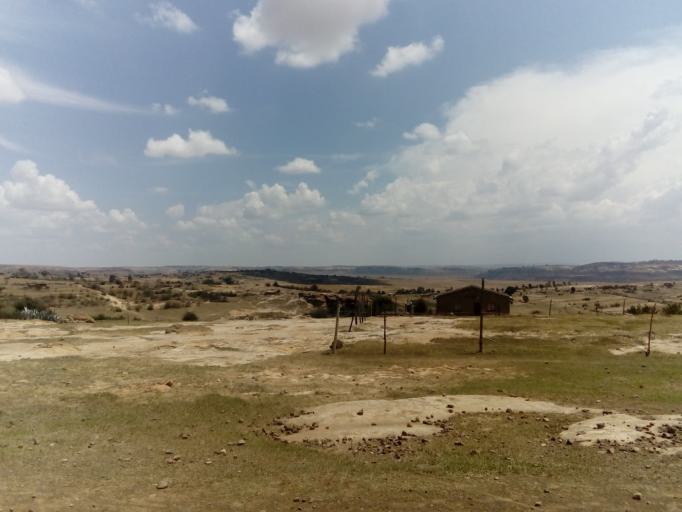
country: LS
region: Berea
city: Teyateyaneng
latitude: -29.1997
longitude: 27.7691
